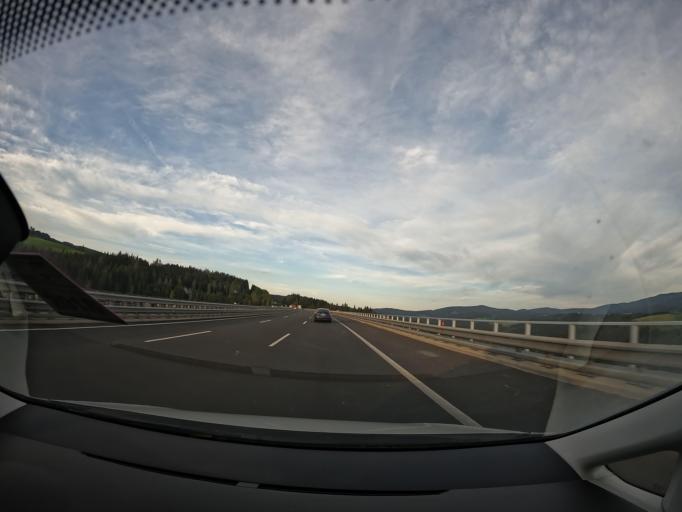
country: AT
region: Carinthia
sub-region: Politischer Bezirk Wolfsberg
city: Preitenegg
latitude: 46.9531
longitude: 14.8867
